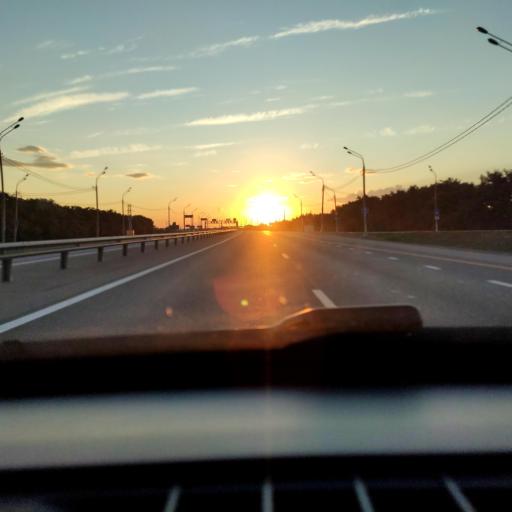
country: RU
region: Lipetsk
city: Khlevnoye
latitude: 52.2162
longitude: 39.1419
